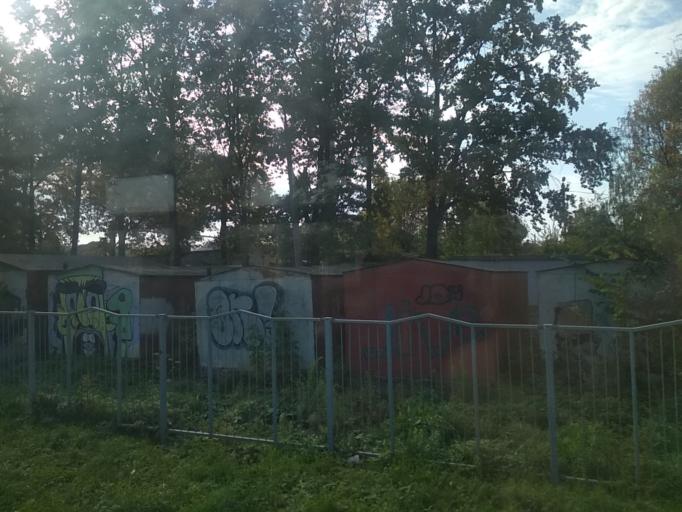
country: BY
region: Minsk
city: Syenitsa
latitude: 53.8452
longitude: 27.5562
